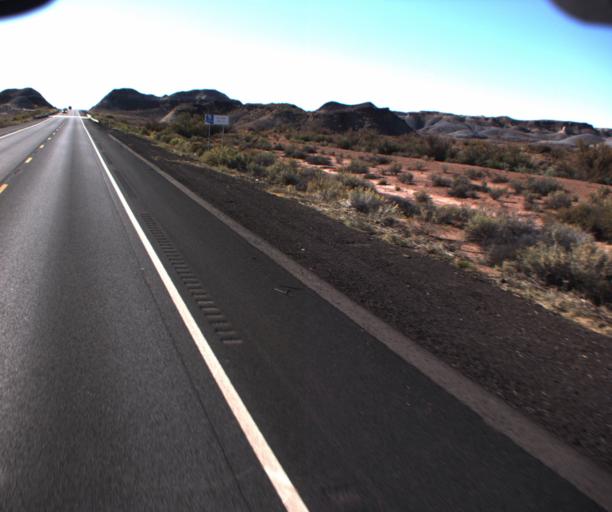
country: US
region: Arizona
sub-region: Coconino County
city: Tuba City
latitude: 36.0934
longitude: -111.3945
